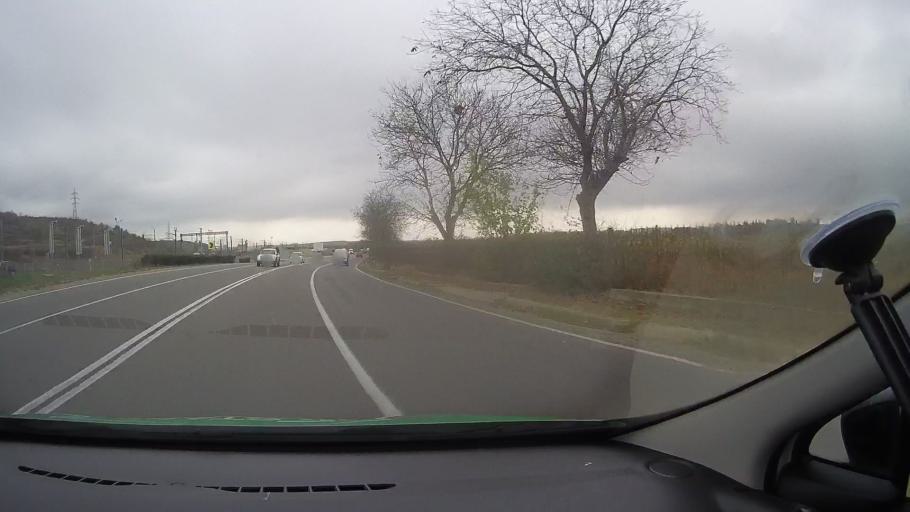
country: RO
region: Constanta
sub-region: Oras Murfatlar
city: Murfatlar
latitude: 44.1710
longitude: 28.4285
